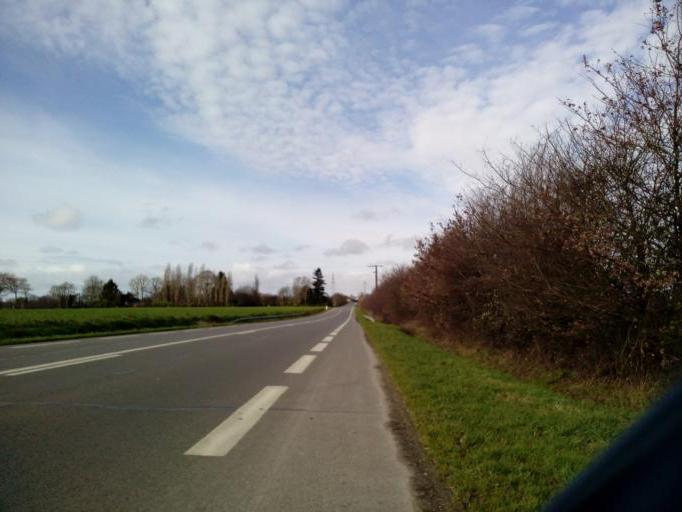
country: FR
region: Brittany
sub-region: Departement d'Ille-et-Vilaine
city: Montgermont
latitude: 48.1628
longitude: -1.7127
